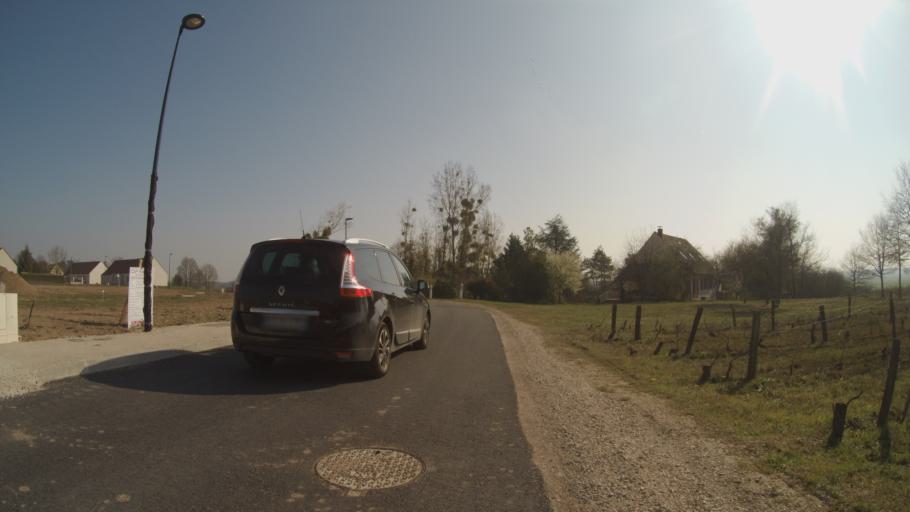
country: FR
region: Centre
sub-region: Departement du Loiret
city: Mardie
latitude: 47.8879
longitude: 2.0491
